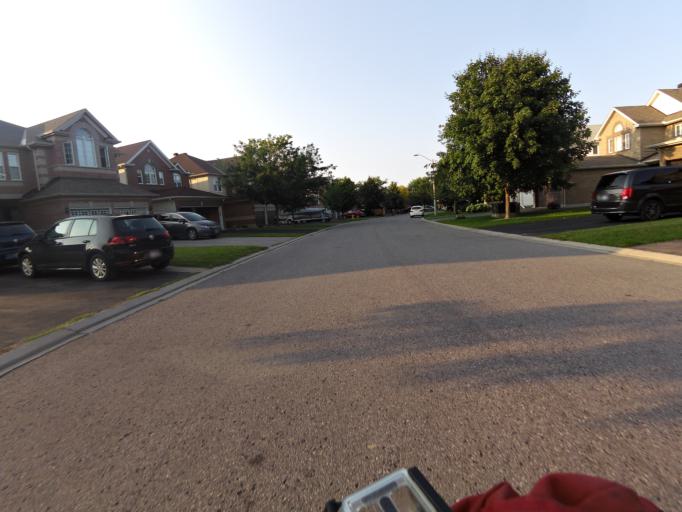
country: CA
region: Ontario
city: Bells Corners
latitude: 45.3554
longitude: -75.9240
